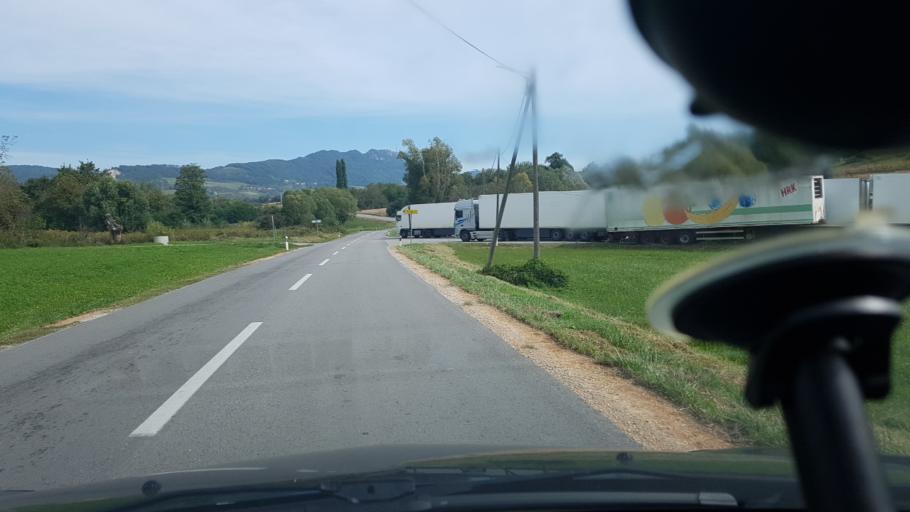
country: HR
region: Varazdinska
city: Ljubescica
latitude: 46.1044
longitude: 16.4144
